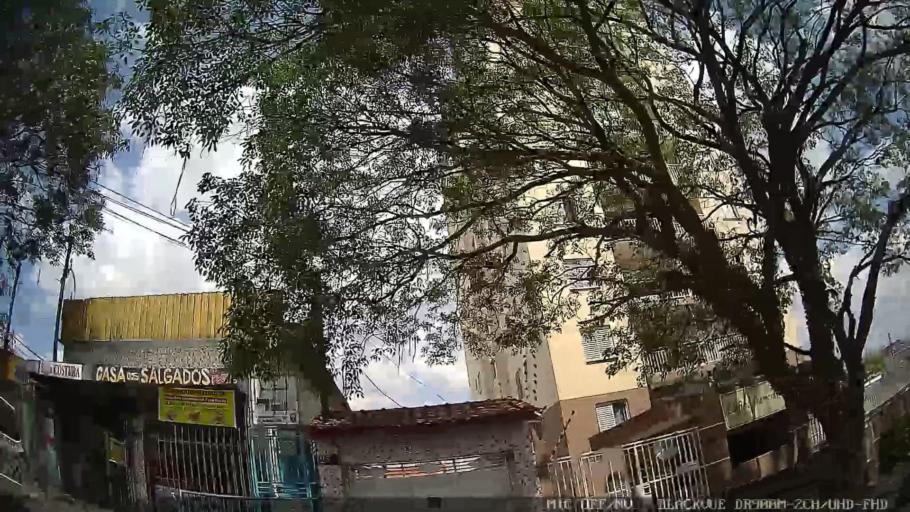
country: BR
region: Sao Paulo
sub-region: Ferraz De Vasconcelos
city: Ferraz de Vasconcelos
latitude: -23.5520
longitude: -46.4577
